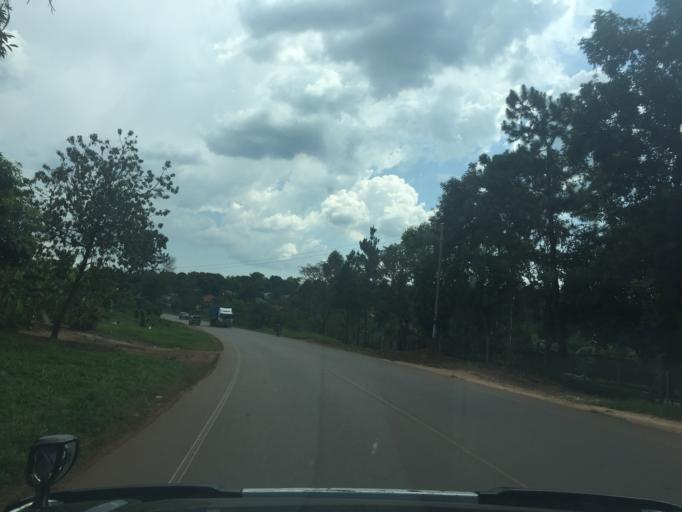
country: UG
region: Central Region
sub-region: Luwero District
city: Wobulenzi
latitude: 0.6999
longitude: 32.5230
